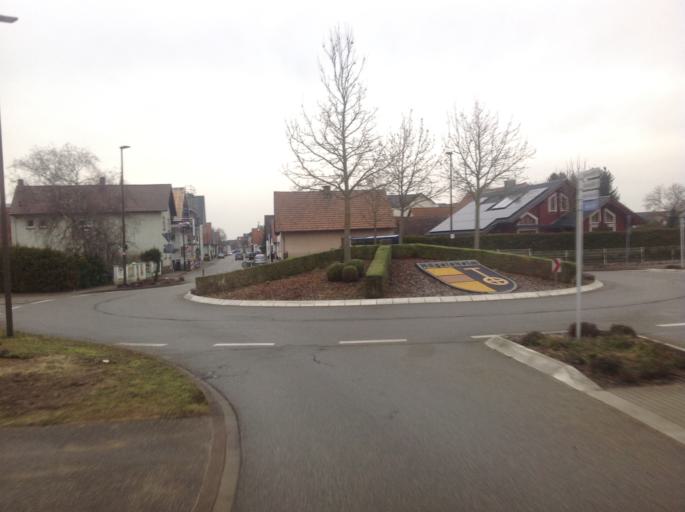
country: DE
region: Baden-Wuerttemberg
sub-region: Karlsruhe Region
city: Hugelsheim
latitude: 48.7957
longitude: 8.1141
